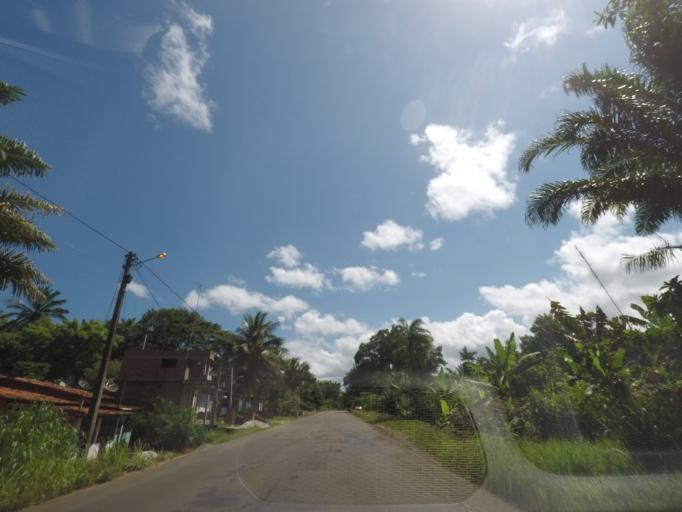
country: BR
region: Bahia
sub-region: Taperoa
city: Taperoa
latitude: -13.4906
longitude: -39.0927
